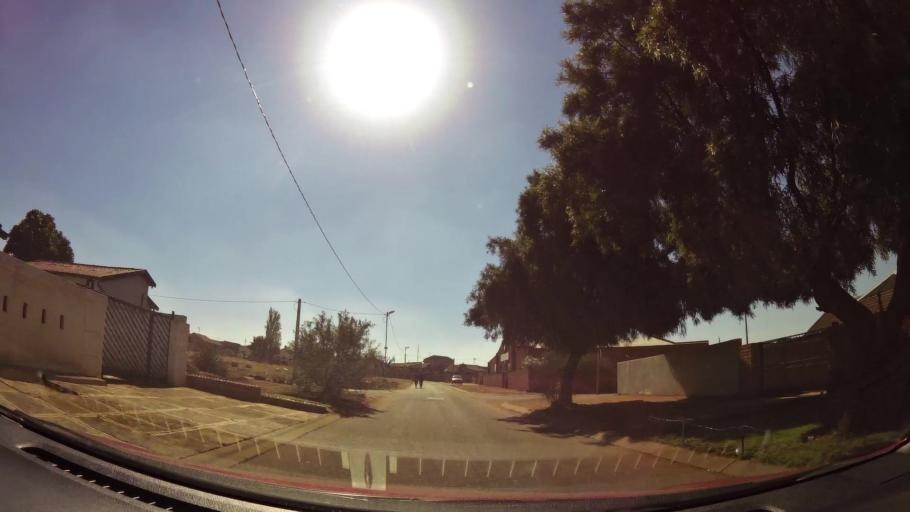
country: ZA
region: Gauteng
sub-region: City of Johannesburg Metropolitan Municipality
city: Soweto
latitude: -26.2492
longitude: 27.8060
